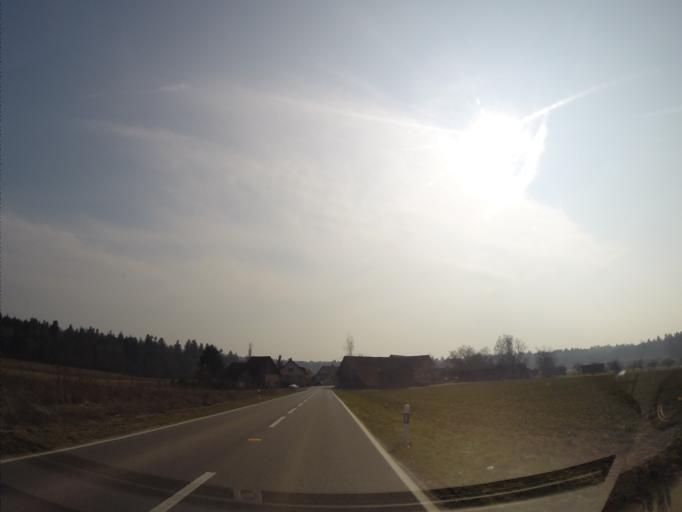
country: CH
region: Thurgau
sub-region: Frauenfeld District
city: Diessenhofen
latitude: 47.6495
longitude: 8.7246
